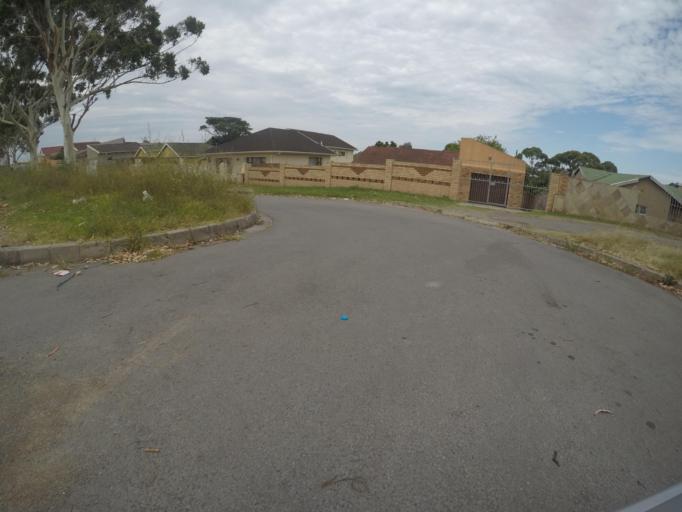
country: ZA
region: Eastern Cape
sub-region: Buffalo City Metropolitan Municipality
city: East London
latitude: -33.0004
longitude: 27.8740
